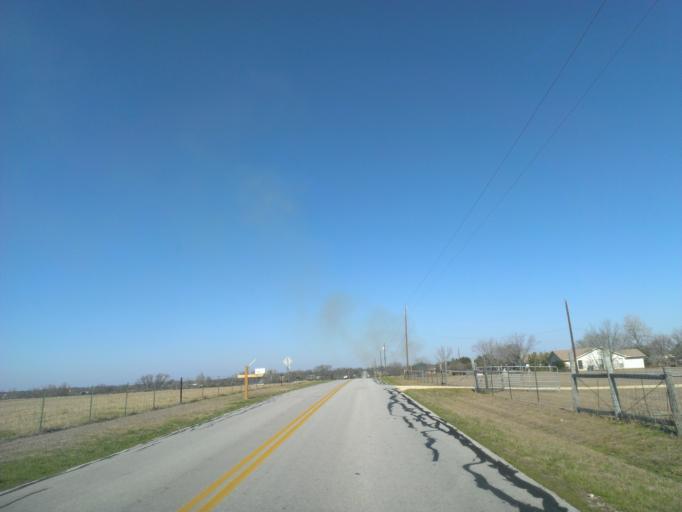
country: US
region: Texas
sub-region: Williamson County
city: Georgetown
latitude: 30.6645
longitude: -97.5816
